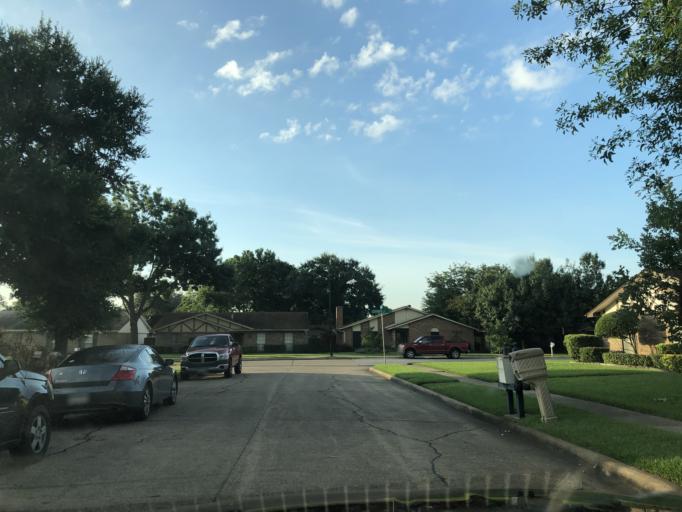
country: US
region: Texas
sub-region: Dallas County
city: Garland
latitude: 32.8482
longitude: -96.6222
